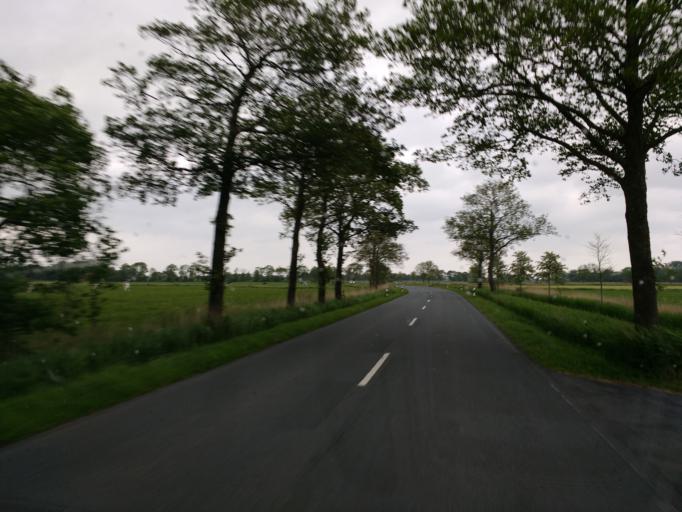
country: DE
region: Lower Saxony
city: Schillig
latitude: 53.6660
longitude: 7.9622
